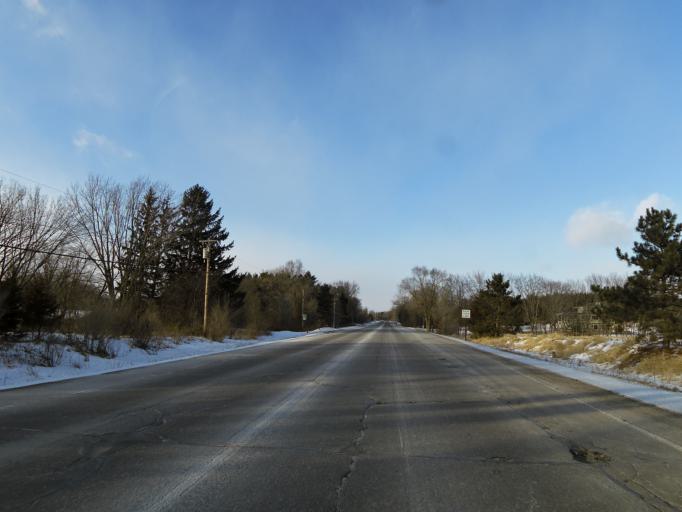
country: US
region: Minnesota
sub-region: Washington County
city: Lake Elmo
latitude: 44.9676
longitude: -92.8831
